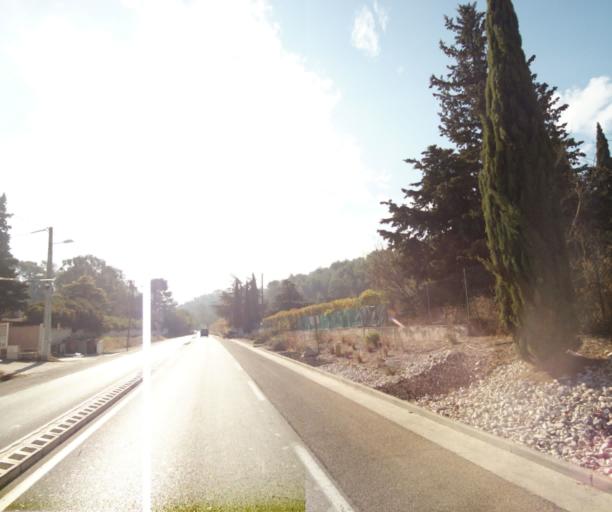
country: FR
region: Provence-Alpes-Cote d'Azur
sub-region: Departement des Bouches-du-Rhone
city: Allauch
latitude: 43.3197
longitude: 5.4941
